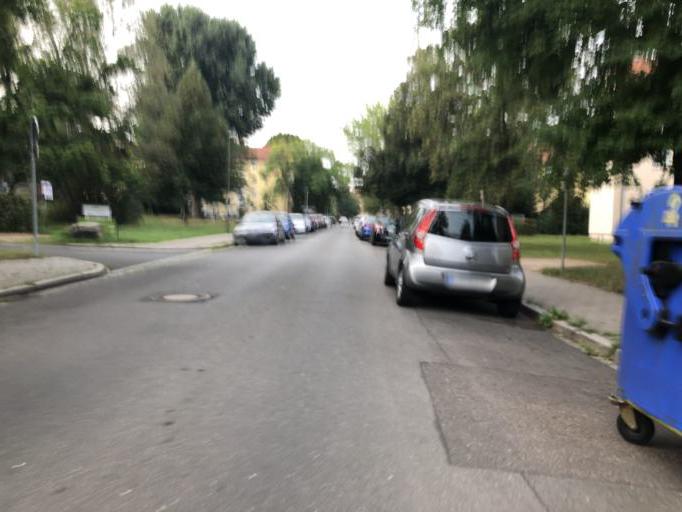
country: DE
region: Bavaria
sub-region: Regierungsbezirk Mittelfranken
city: Erlangen
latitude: 49.5825
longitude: 10.9969
